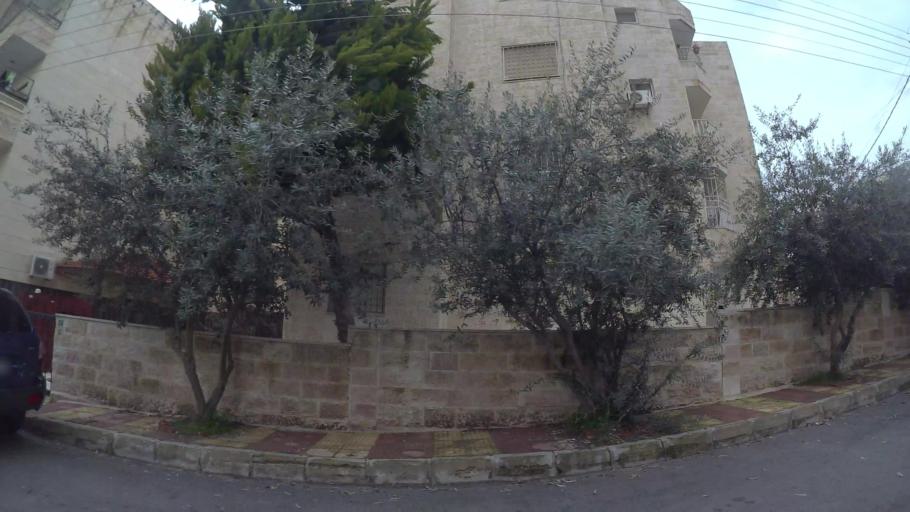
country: JO
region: Amman
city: Umm as Summaq
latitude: 31.9003
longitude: 35.8454
